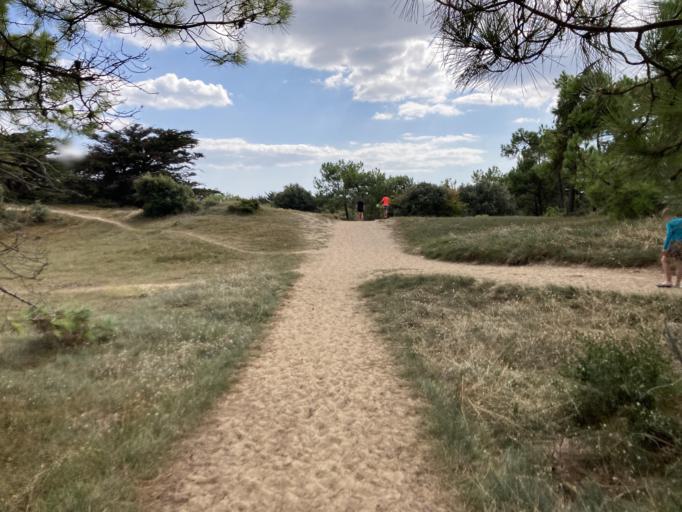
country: FR
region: Pays de la Loire
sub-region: Departement de la Vendee
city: Le Perrier
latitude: 46.7487
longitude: -2.0149
